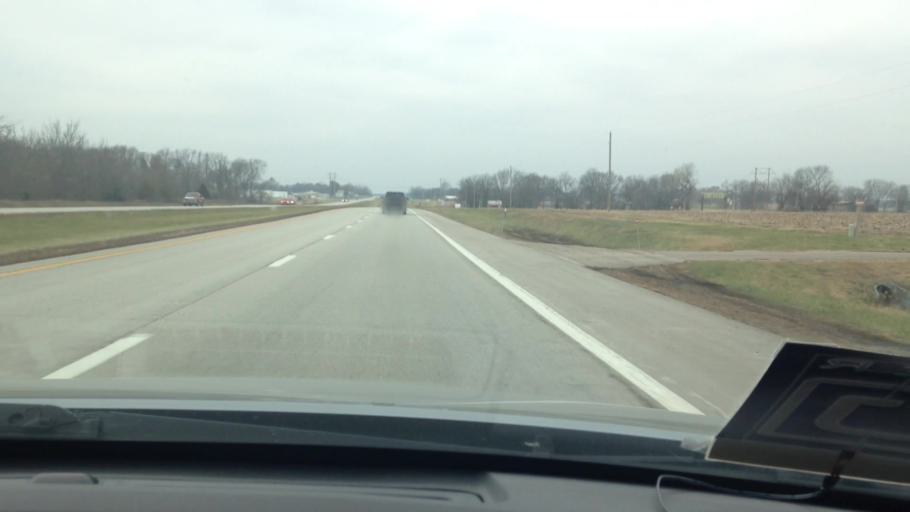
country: US
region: Missouri
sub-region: Cass County
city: Garden City
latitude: 38.5912
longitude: -94.2397
